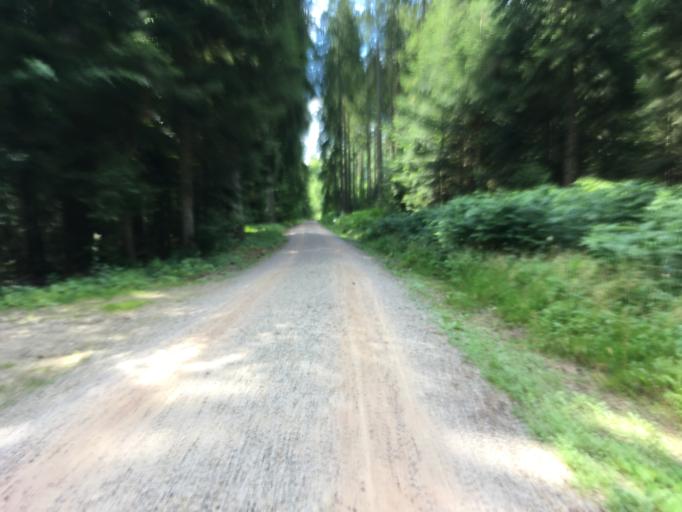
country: DE
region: Baden-Wuerttemberg
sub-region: Karlsruhe Region
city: Lossburg
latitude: 48.4259
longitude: 8.4391
